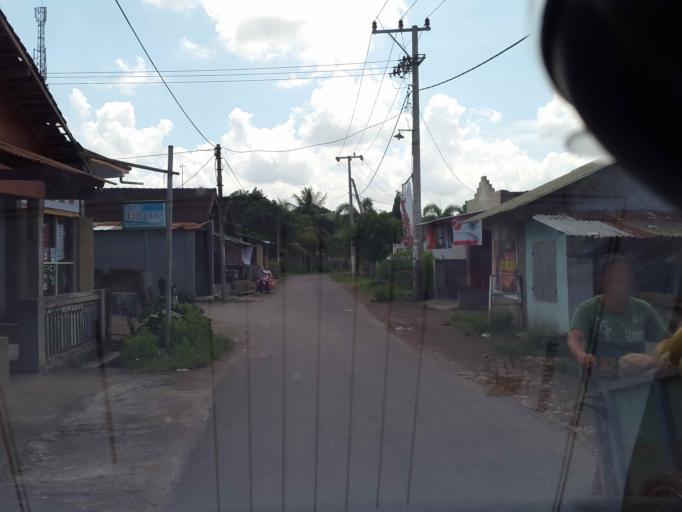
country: ID
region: West Nusa Tenggara
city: Mambalan
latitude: -8.5291
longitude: 116.0776
